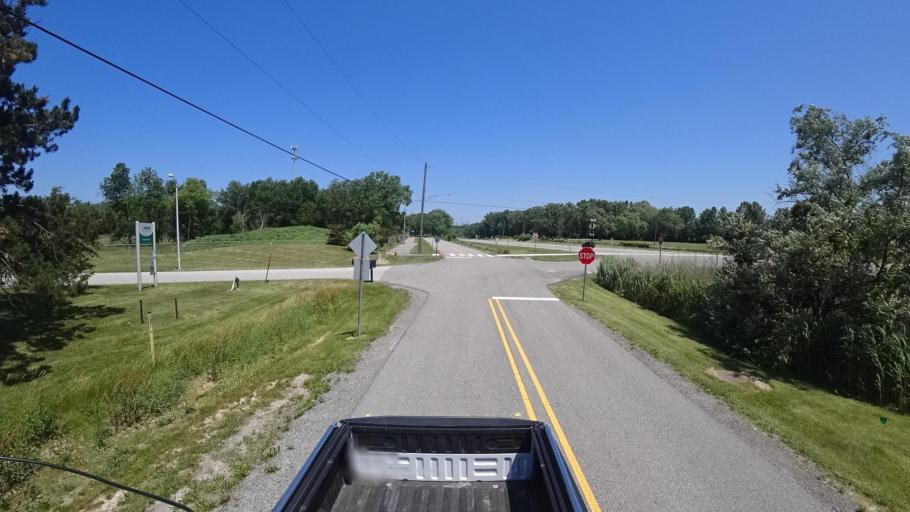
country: US
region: Indiana
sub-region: Porter County
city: Burns Harbor
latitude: 41.6101
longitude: -87.1261
